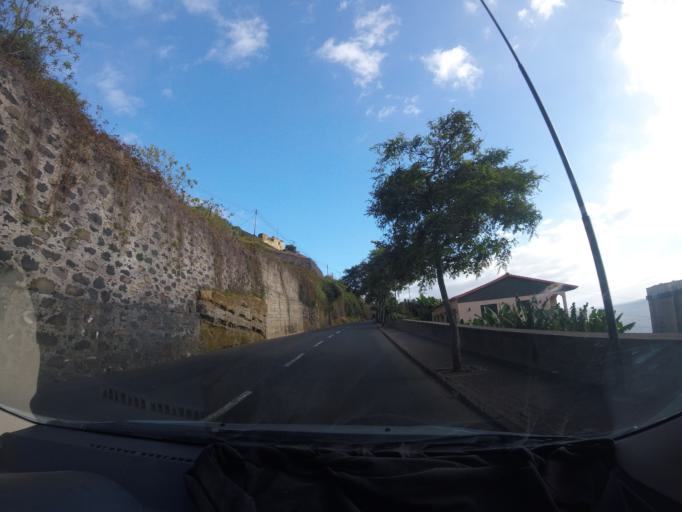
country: PT
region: Madeira
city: Camara de Lobos
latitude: 32.6456
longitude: -16.9653
